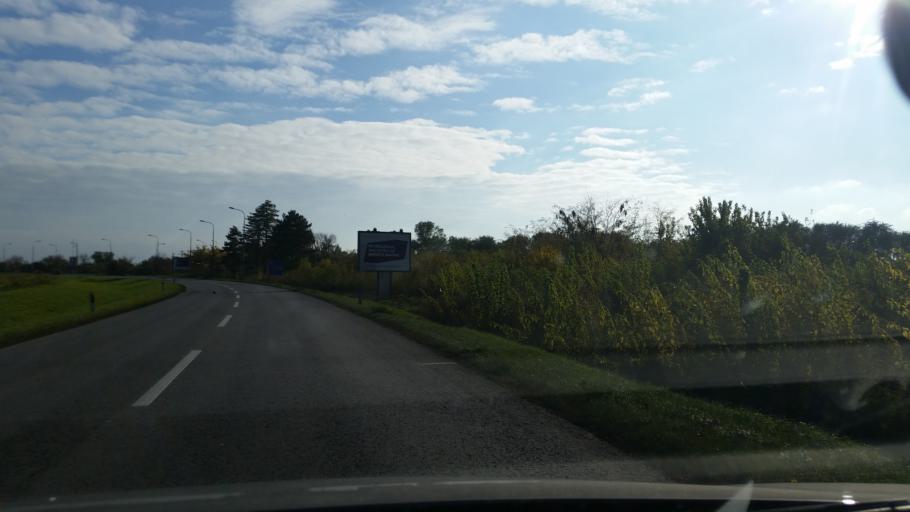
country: RS
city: Ecka
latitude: 45.3541
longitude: 20.4189
